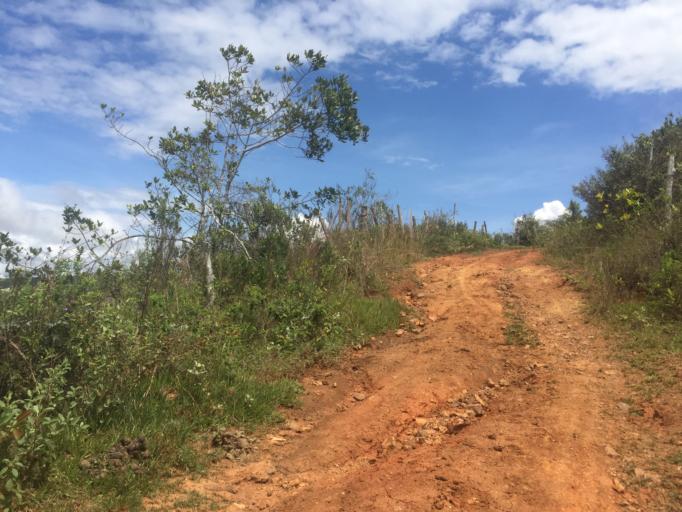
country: CO
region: Valle del Cauca
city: Dagua
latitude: 3.7135
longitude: -76.6029
